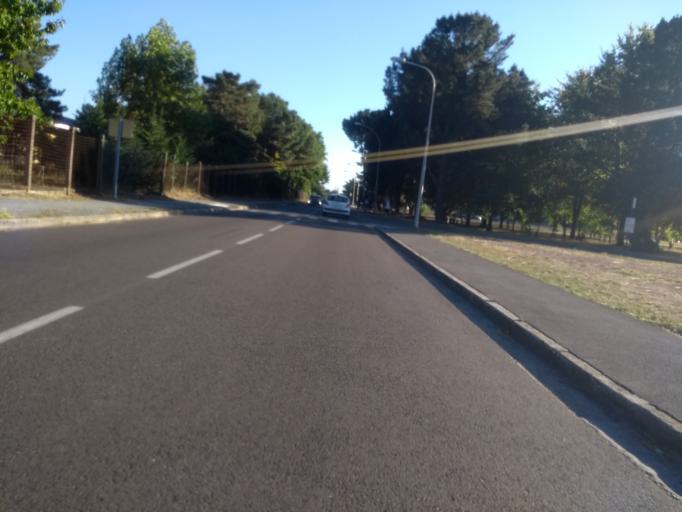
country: FR
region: Aquitaine
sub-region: Departement de la Gironde
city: Gradignan
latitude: 44.7933
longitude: -0.6134
